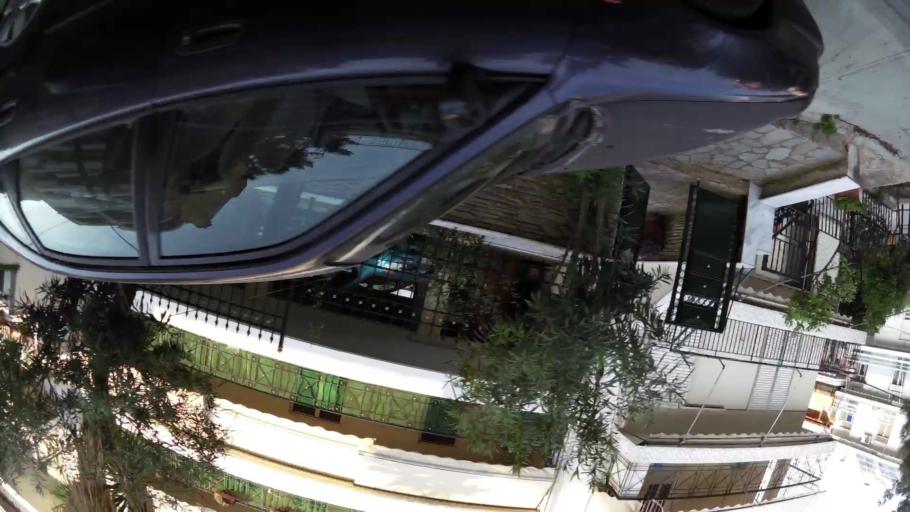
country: GR
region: Attica
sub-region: Nomarchia Athinas
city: Petroupolis
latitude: 38.0409
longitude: 23.6749
